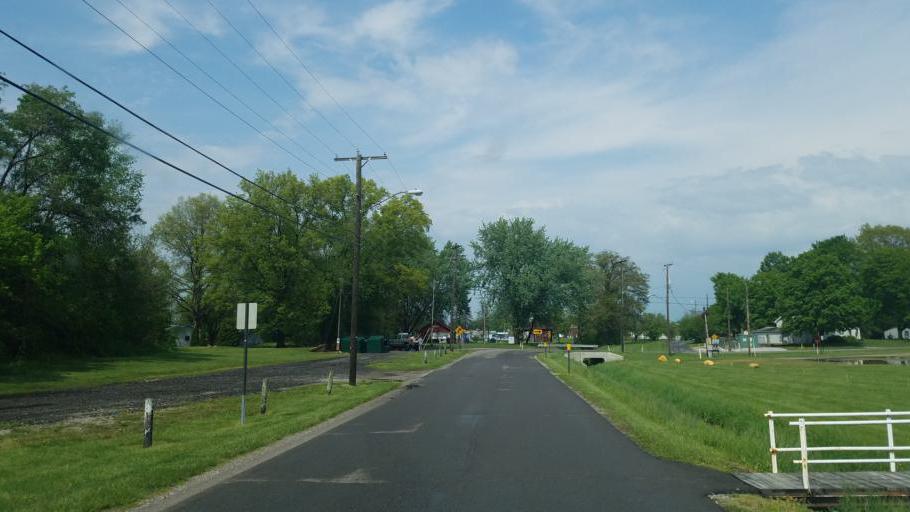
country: US
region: Ohio
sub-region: Licking County
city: Hebron
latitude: 39.9584
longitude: -82.4942
